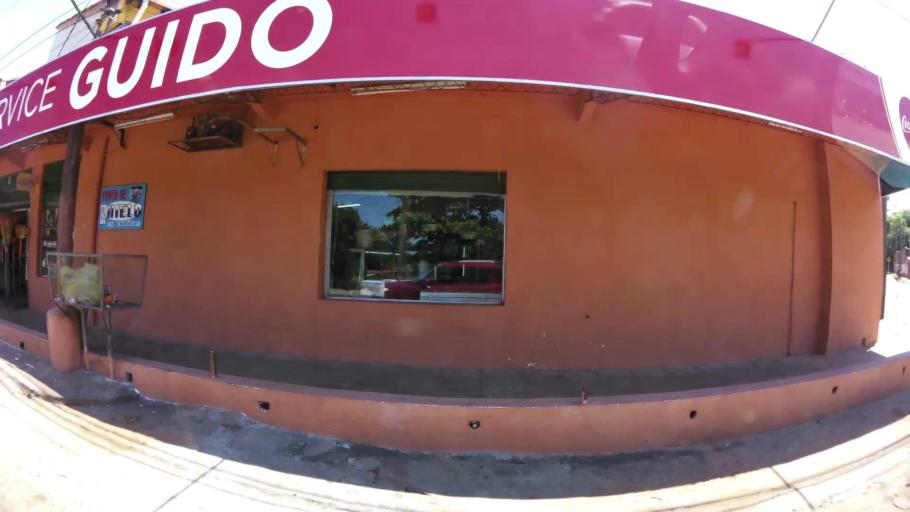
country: PY
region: Central
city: San Antonio
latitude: -25.4084
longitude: -57.5460
